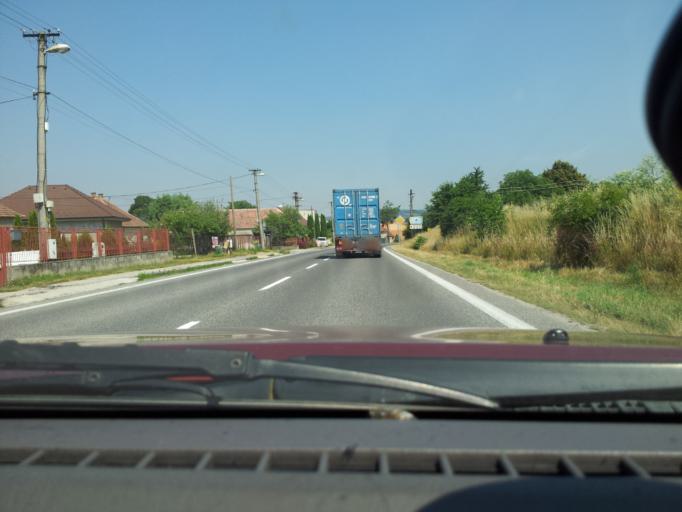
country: SK
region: Trnavsky
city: Smolenice
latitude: 48.4996
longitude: 17.4819
